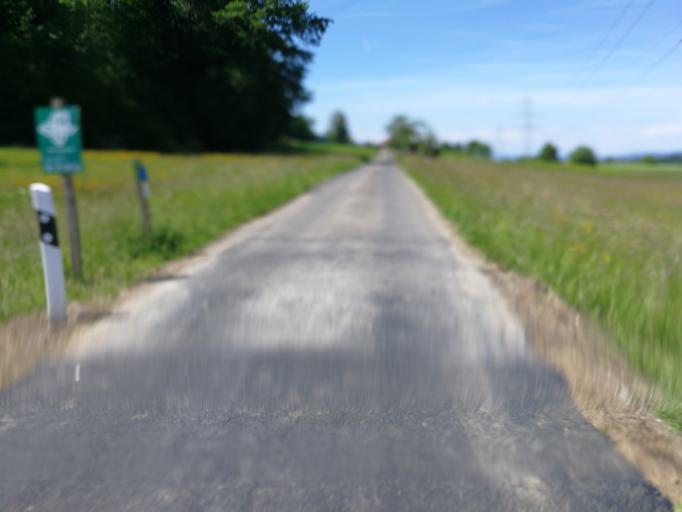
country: CH
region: Zurich
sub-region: Bezirk Horgen
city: Waedenswil / Untermosen-Fuhr
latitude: 47.2053
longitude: 8.6450
